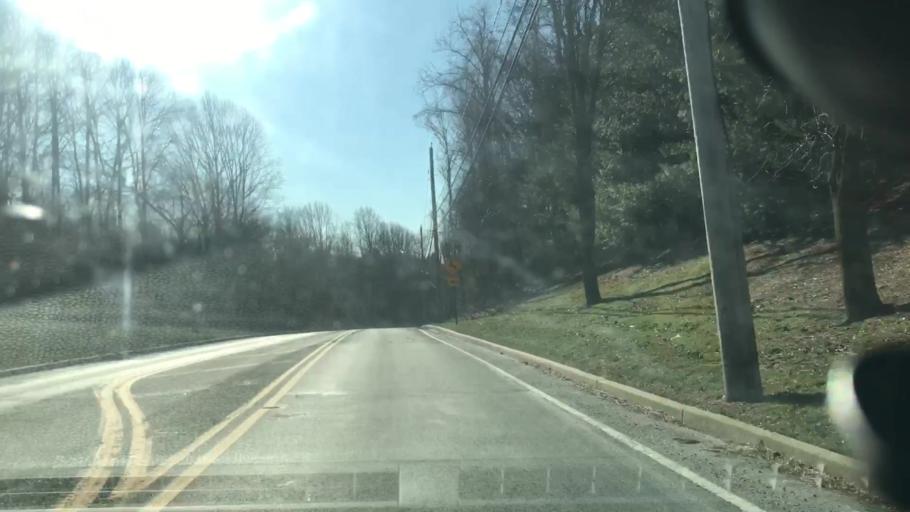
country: US
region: New Jersey
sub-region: Monmouth County
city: Keansburg
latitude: 40.3882
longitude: -74.1456
